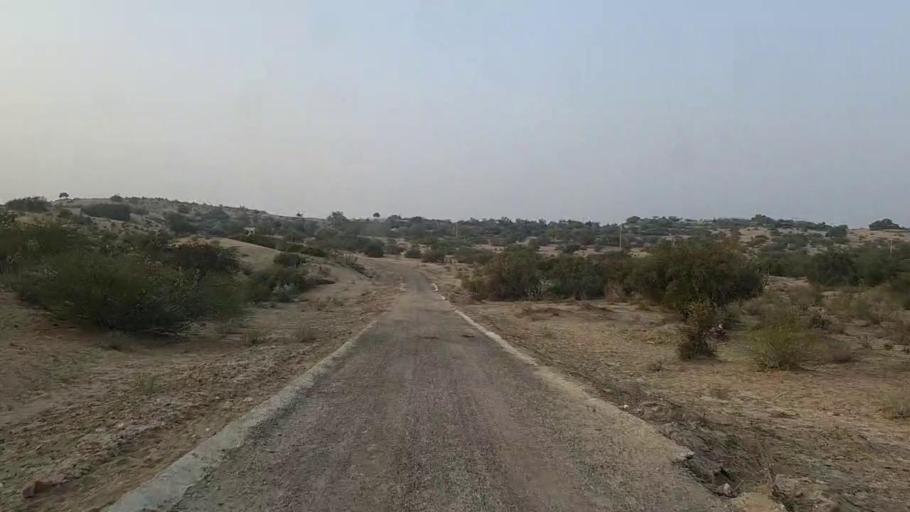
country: PK
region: Sindh
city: Naukot
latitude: 24.6794
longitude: 69.4589
